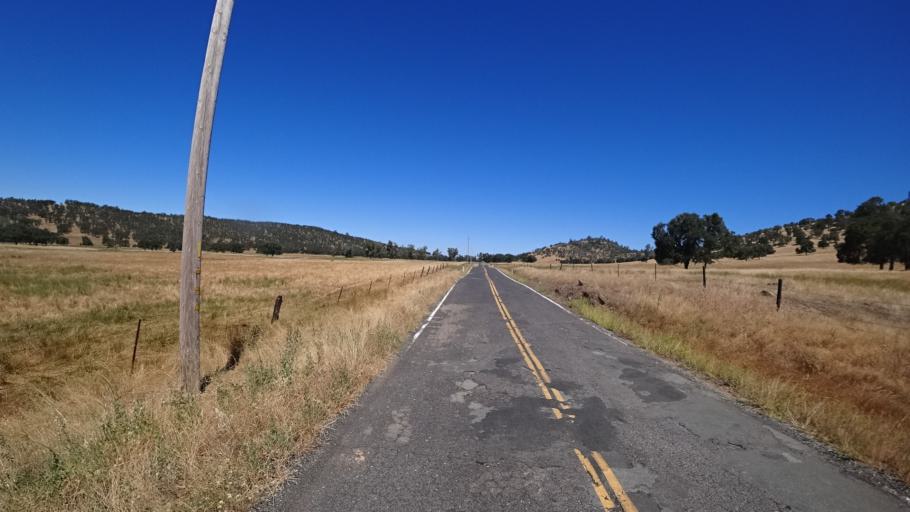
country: US
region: California
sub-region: Calaveras County
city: Copperopolis
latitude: 38.0123
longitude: -120.6722
